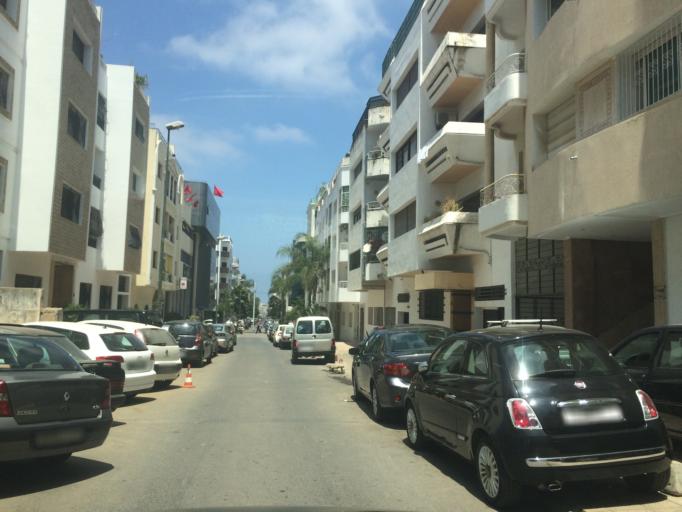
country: MA
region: Rabat-Sale-Zemmour-Zaer
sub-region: Rabat
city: Rabat
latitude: 33.9971
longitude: -6.8468
